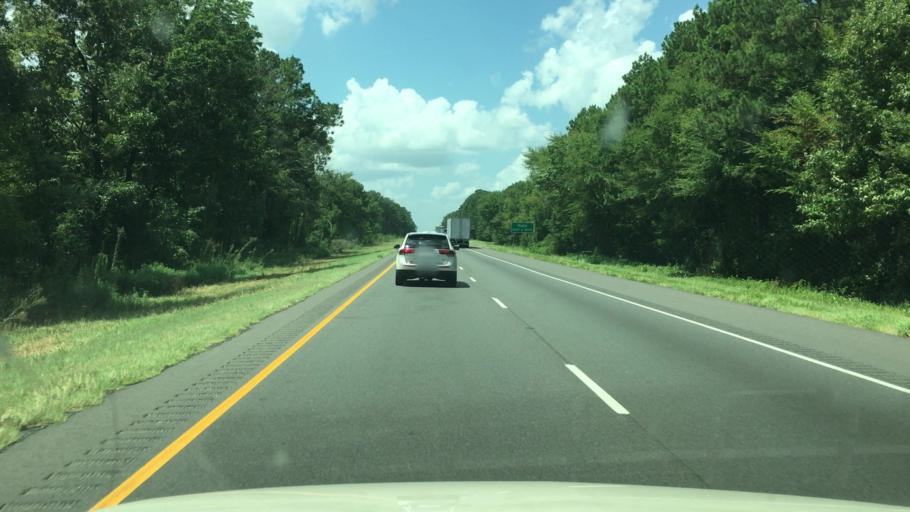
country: US
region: Arkansas
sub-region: Hempstead County
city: Hope
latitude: 33.7134
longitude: -93.5679
